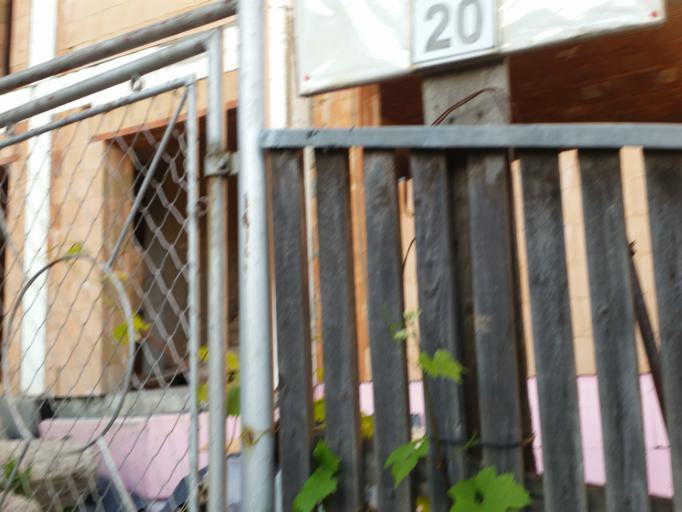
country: RO
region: Cluj
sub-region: Municipiul Cluj-Napoca
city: Cluj-Napoca
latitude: 46.7748
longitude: 23.5709
